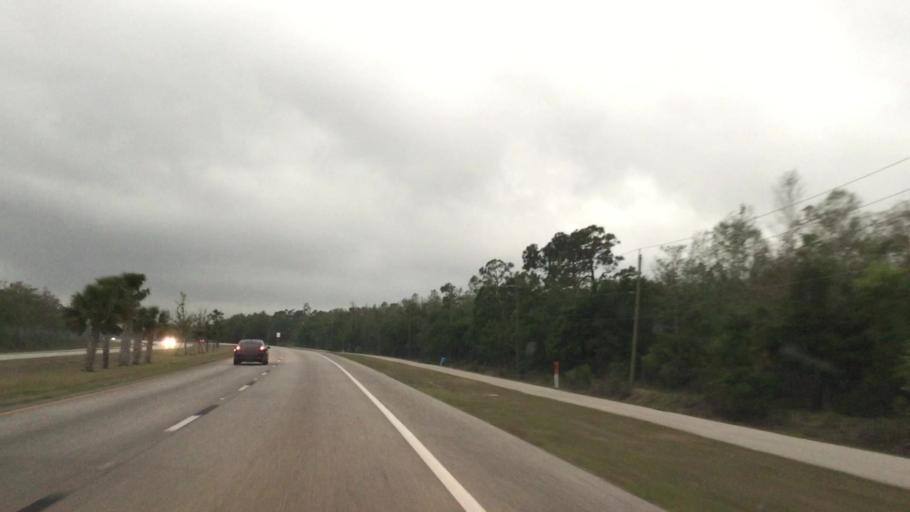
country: US
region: Florida
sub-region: Lee County
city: Fort Myers
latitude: 26.5816
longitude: -81.8230
